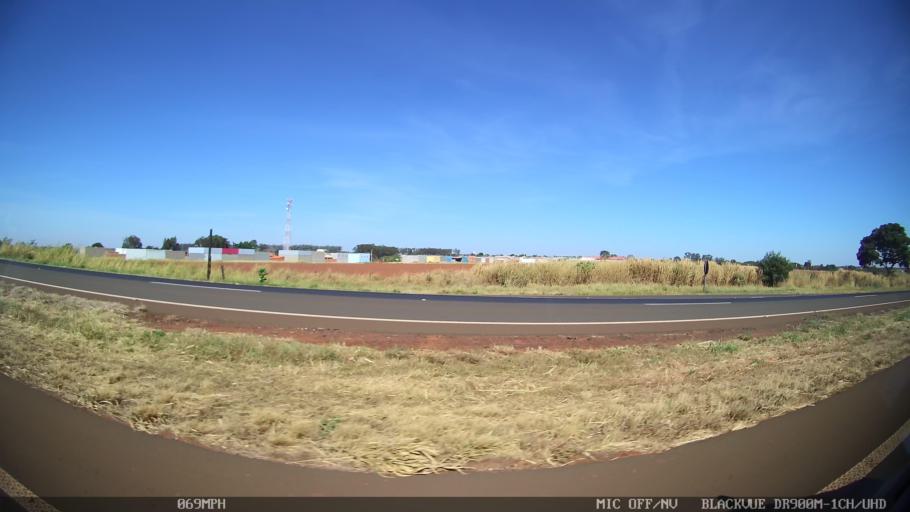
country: BR
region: Sao Paulo
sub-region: Barretos
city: Barretos
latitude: -20.5170
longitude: -48.5711
